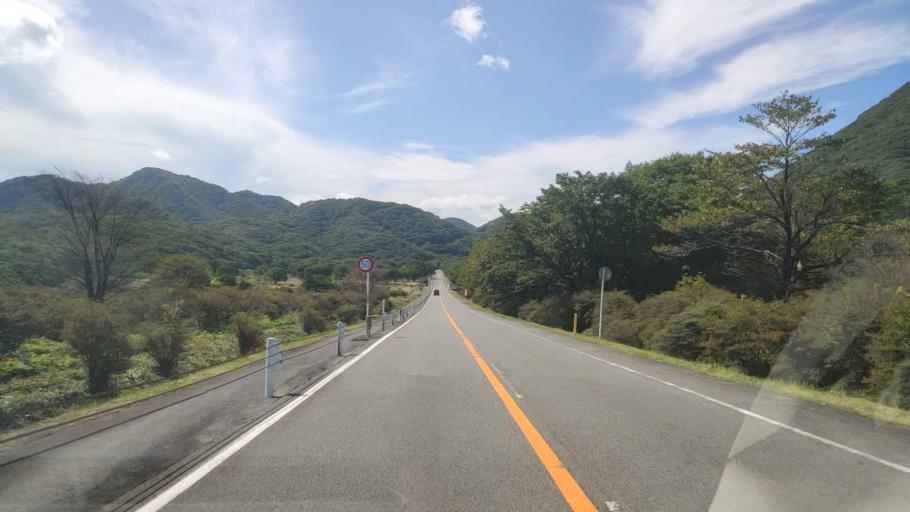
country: JP
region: Gunma
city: Shibukawa
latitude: 36.4766
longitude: 138.8900
